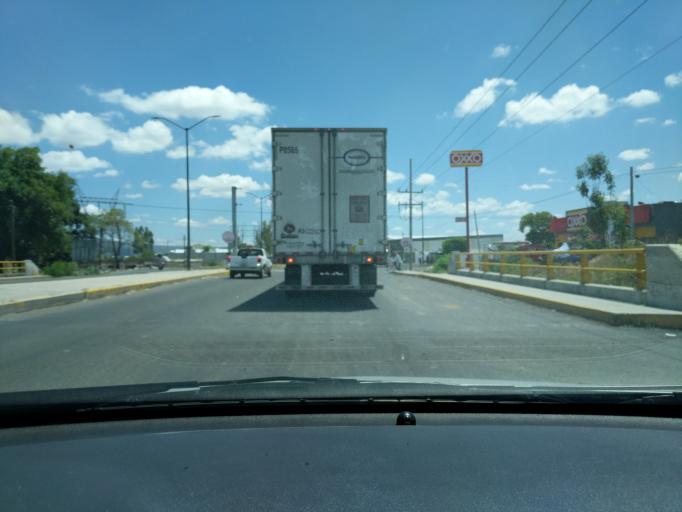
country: MX
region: Guanajuato
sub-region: Salamanca
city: El Divisador
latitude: 20.6025
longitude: -101.1766
